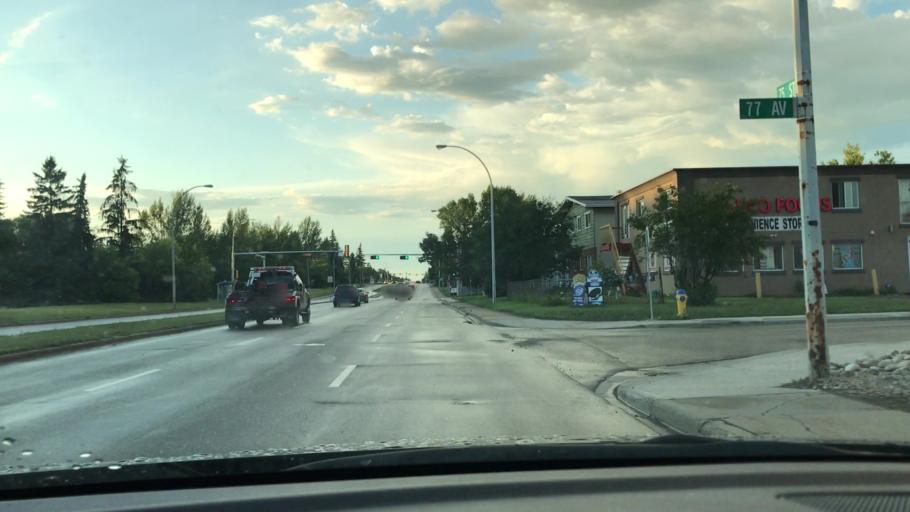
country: CA
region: Alberta
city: Edmonton
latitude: 53.5131
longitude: -113.4428
